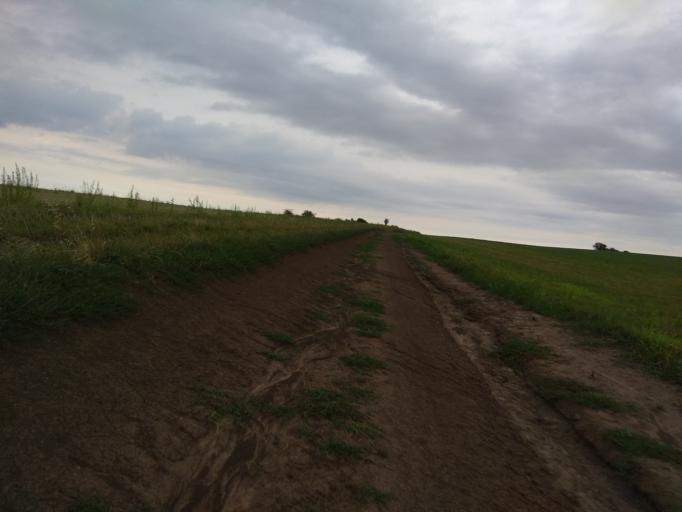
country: HU
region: Borsod-Abauj-Zemplen
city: Megyaszo
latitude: 48.1786
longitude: 21.0992
